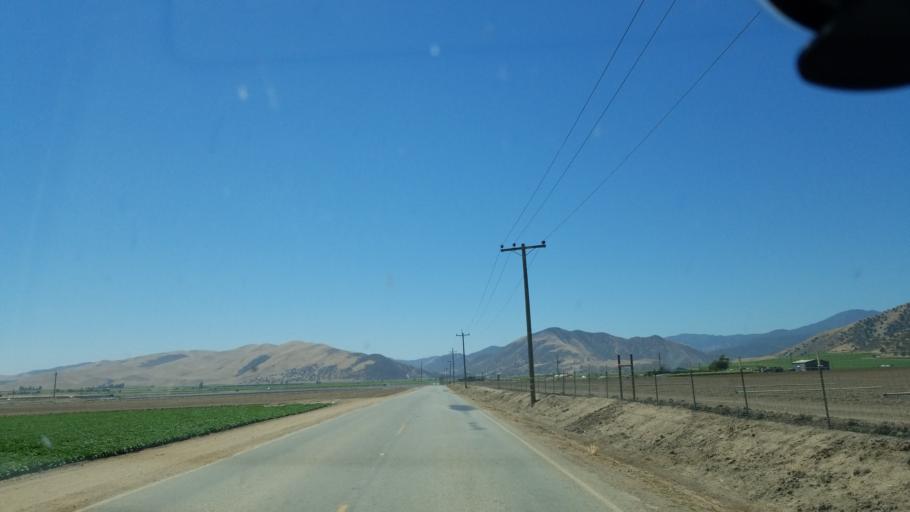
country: US
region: California
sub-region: Monterey County
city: Greenfield
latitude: 36.3311
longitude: -121.3156
